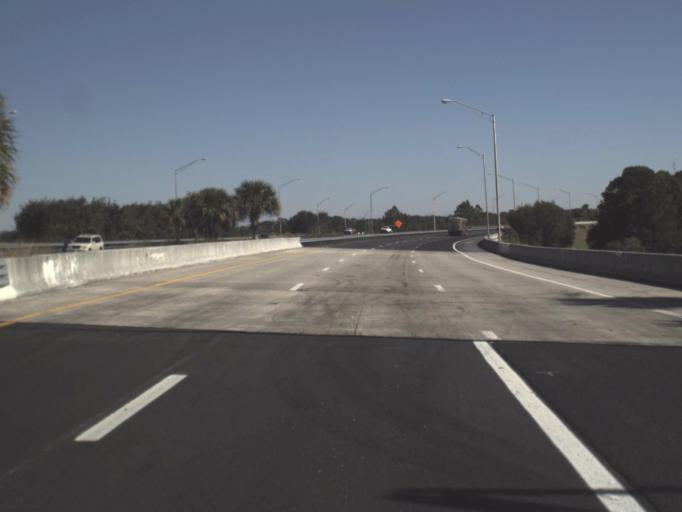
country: US
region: Florida
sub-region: Seminole County
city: Sanford
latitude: 28.7711
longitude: -81.2804
